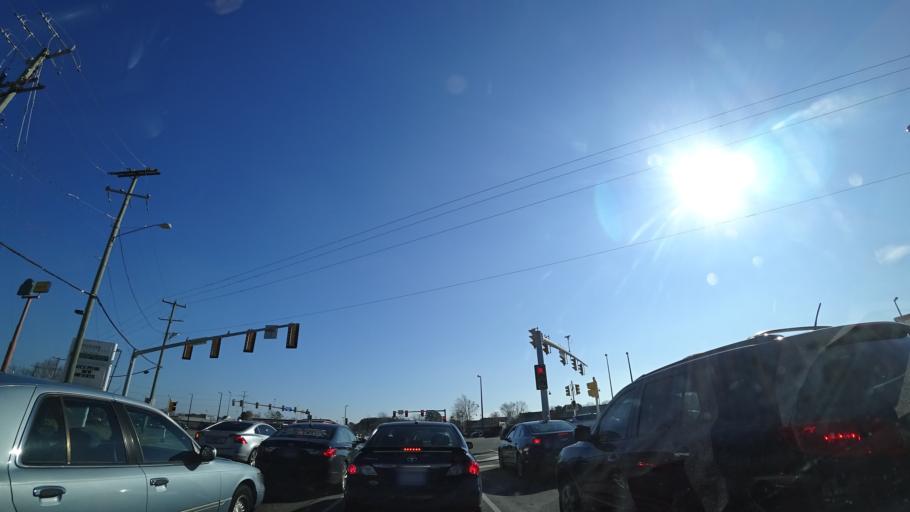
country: US
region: Virginia
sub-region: City of Hampton
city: Hampton
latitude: 37.0396
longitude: -76.4015
